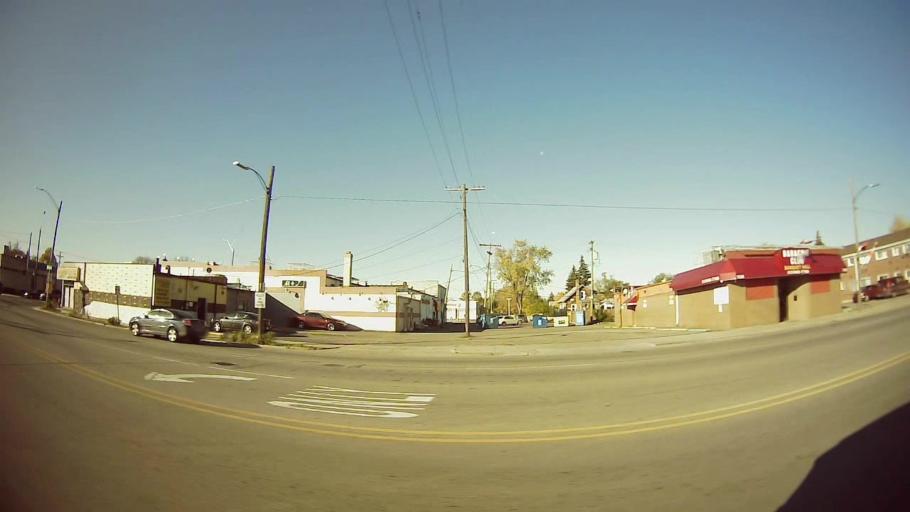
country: US
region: Michigan
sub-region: Wayne County
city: Dearborn
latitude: 42.3442
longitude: -83.1962
